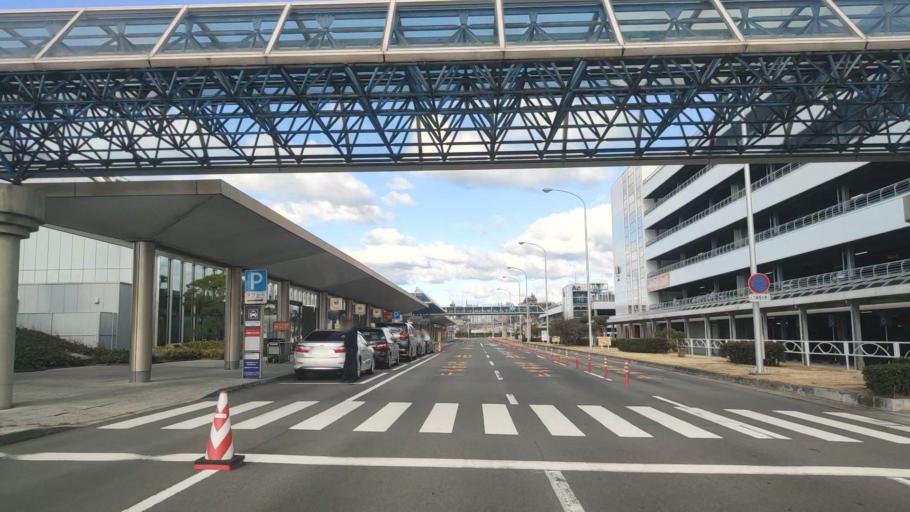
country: JP
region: Ehime
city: Masaki-cho
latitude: 33.8286
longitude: 132.7054
